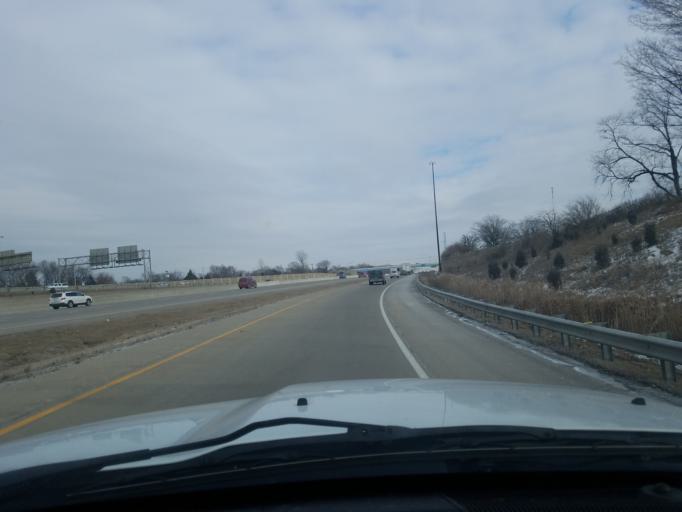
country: US
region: Indiana
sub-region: Marion County
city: Warren Park
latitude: 39.7986
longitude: -86.0306
